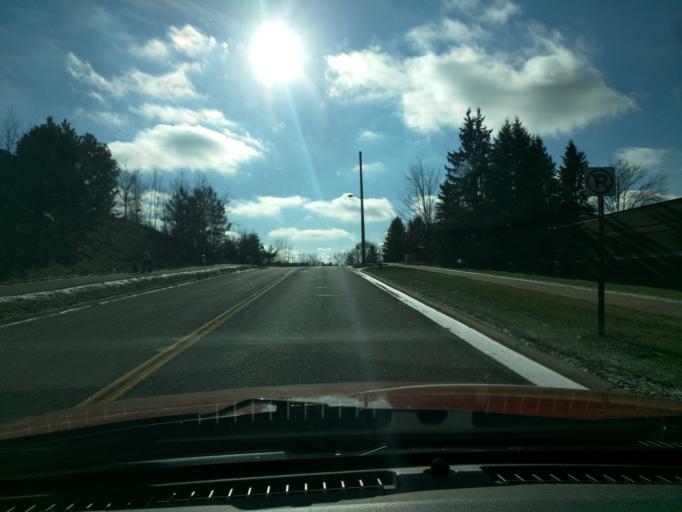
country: US
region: Minnesota
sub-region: Hennepin County
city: Eden Prairie
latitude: 44.8707
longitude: -93.4139
